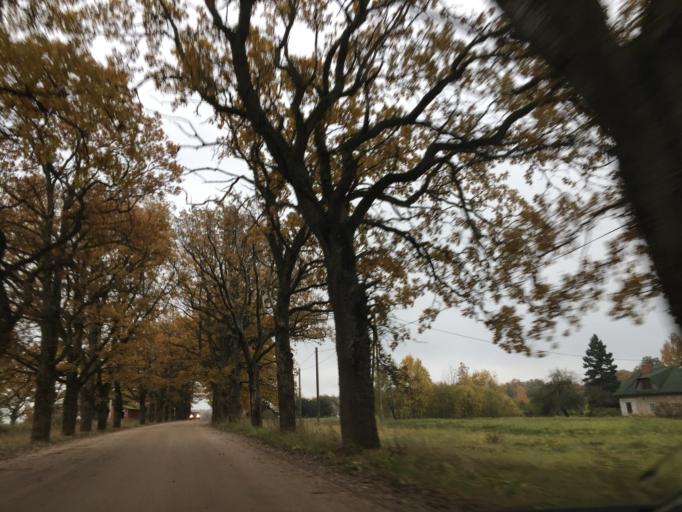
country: LV
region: Sigulda
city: Sigulda
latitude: 57.2660
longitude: 24.8713
